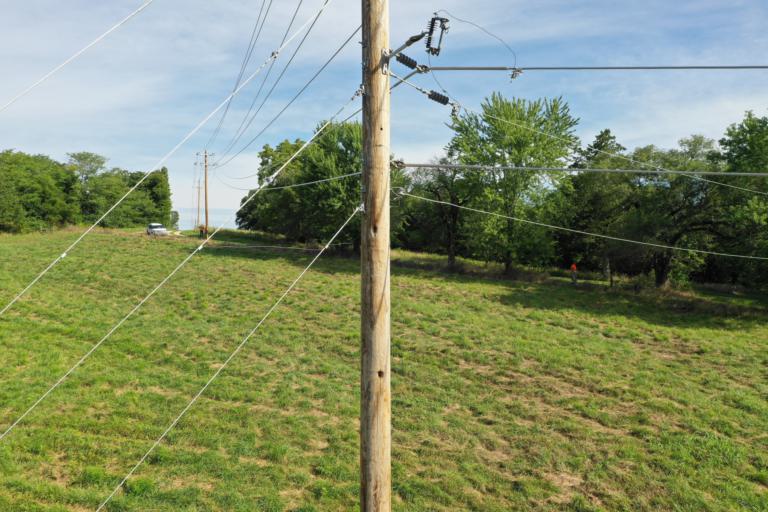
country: US
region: Missouri
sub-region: Callaway County
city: Holts Summit
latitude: 38.5348
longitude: -92.0514
